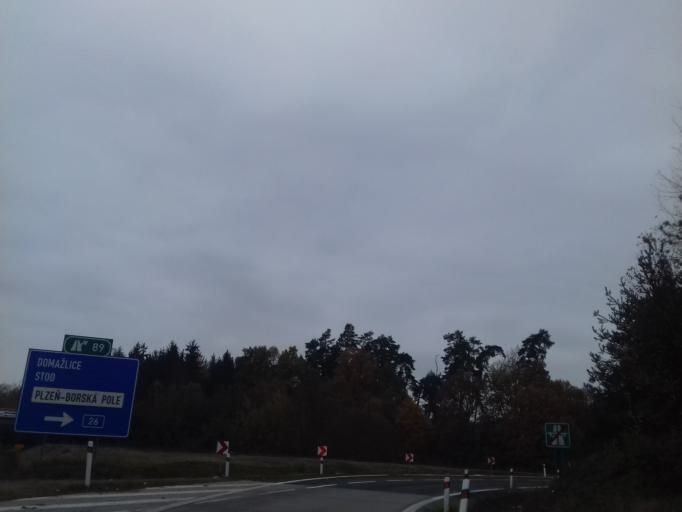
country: CZ
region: Plzensky
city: Vejprnice
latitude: 49.7091
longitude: 13.2802
